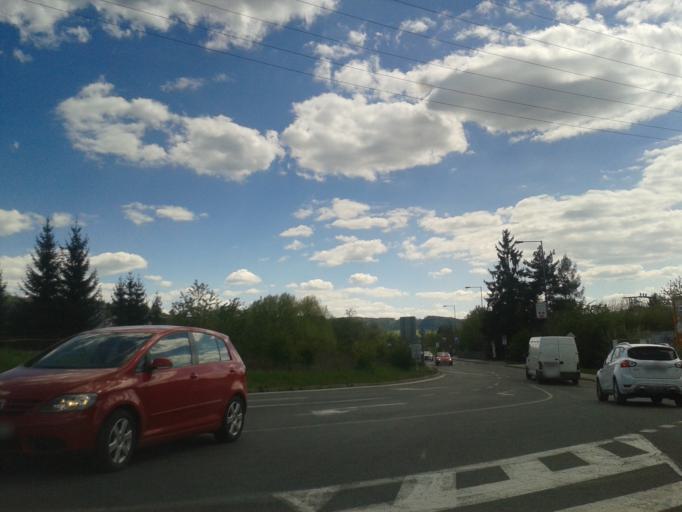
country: CZ
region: Central Bohemia
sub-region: Okres Beroun
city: Beroun
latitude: 49.9797
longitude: 14.0749
